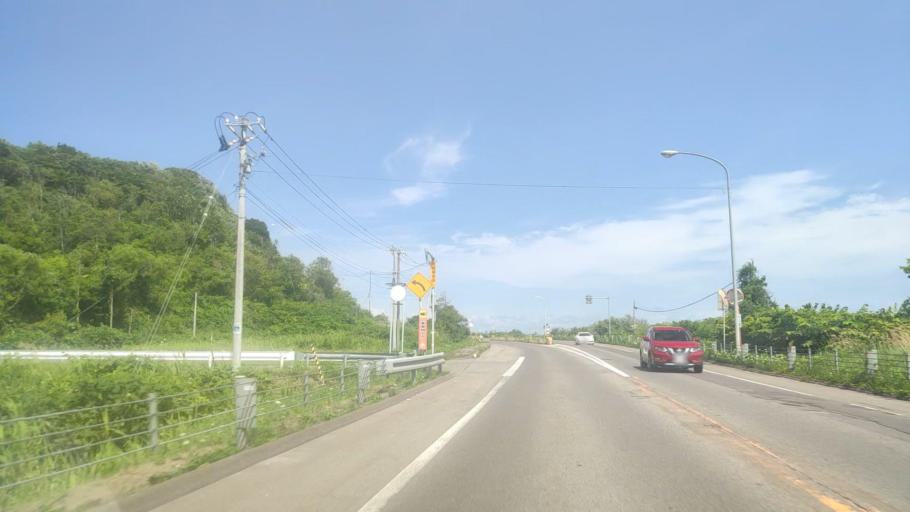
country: JP
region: Hokkaido
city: Nanae
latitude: 42.1957
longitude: 140.4199
